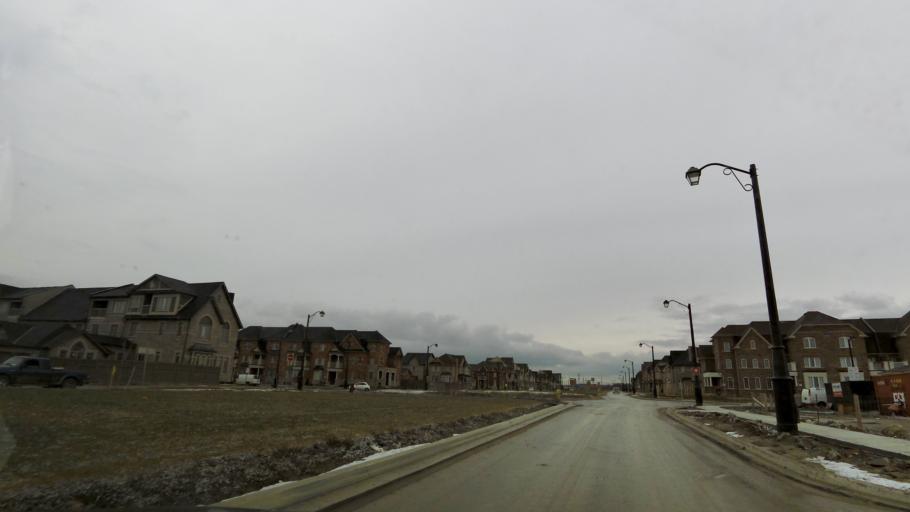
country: CA
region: Ontario
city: Vaughan
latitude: 43.8324
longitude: -79.6560
